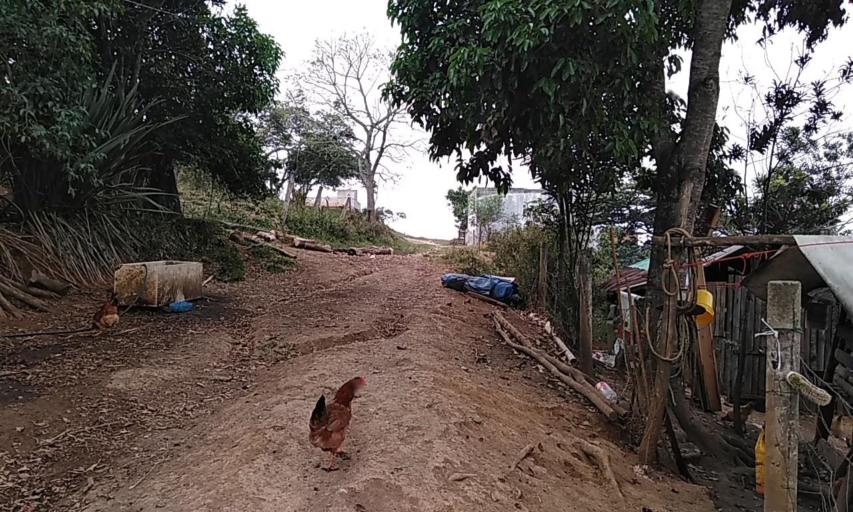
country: MX
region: Veracruz
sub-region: Xalapa
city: Fraccionamiento las Fuentes
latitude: 19.4908
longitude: -96.8961
